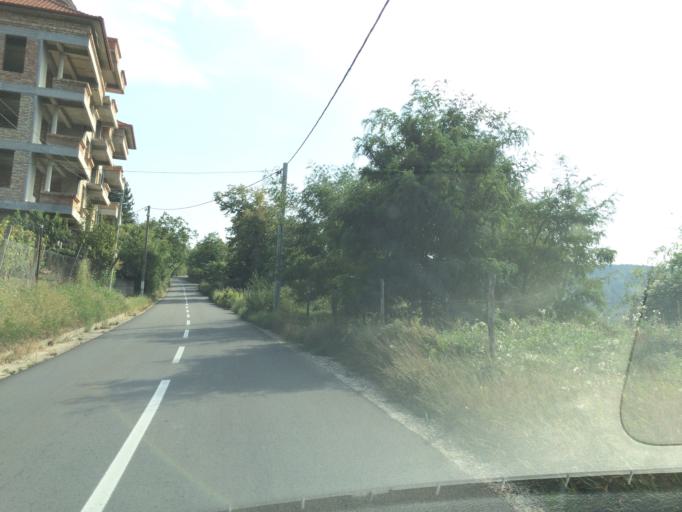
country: RS
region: Autonomna Pokrajina Vojvodina
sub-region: Juznobacki Okrug
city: Novi Sad
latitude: 45.1960
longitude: 19.8331
